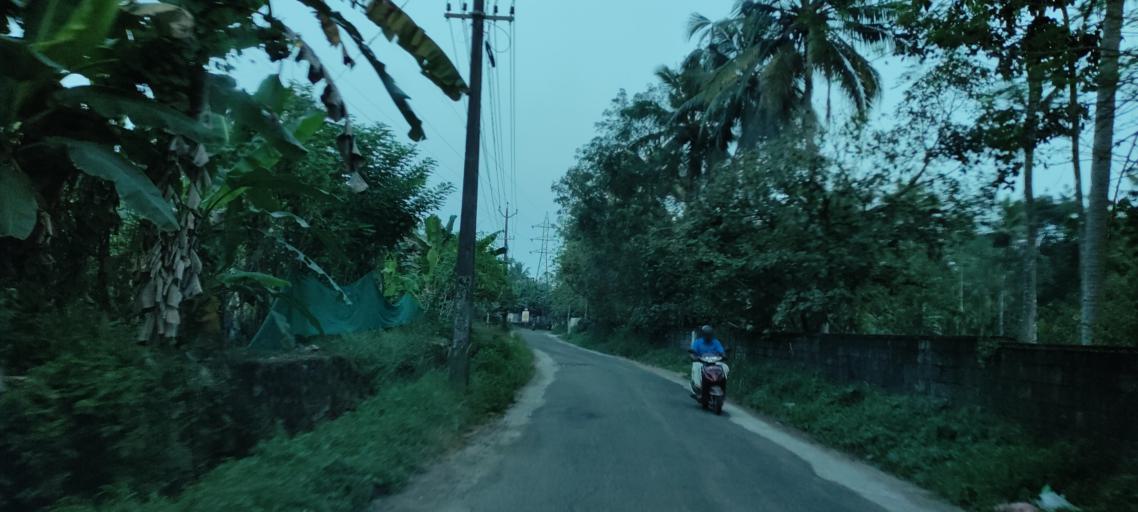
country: IN
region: Kerala
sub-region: Pattanamtitta
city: Adur
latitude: 9.1602
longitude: 76.7392
